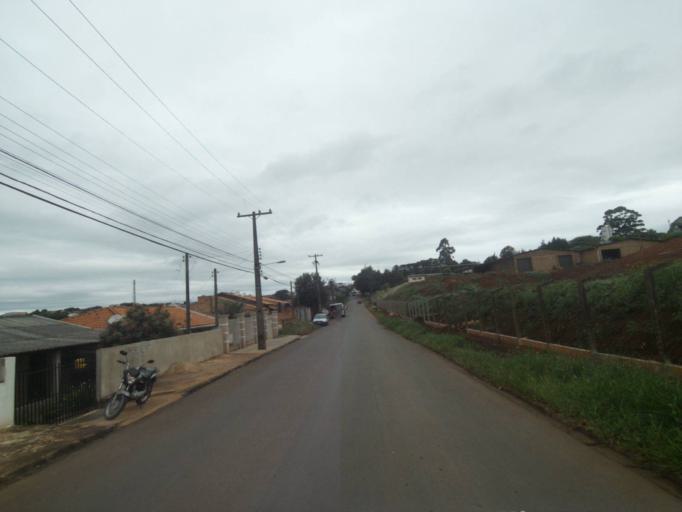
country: BR
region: Parana
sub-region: Telemaco Borba
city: Telemaco Borba
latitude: -24.3269
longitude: -50.6504
